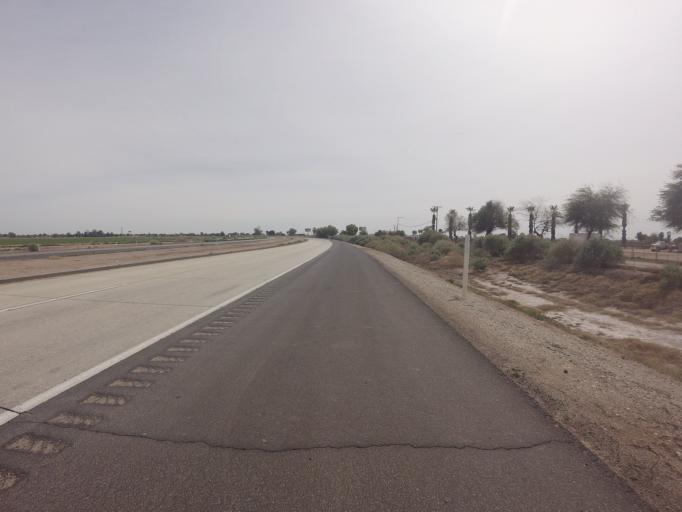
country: US
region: California
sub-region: Imperial County
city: Brawley
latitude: 32.9838
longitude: -115.5774
